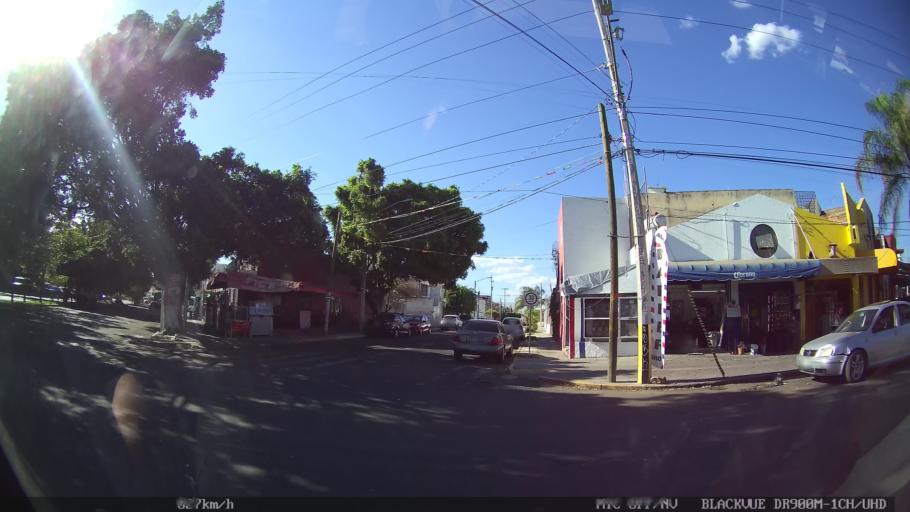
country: MX
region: Jalisco
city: Tlaquepaque
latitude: 20.7122
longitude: -103.3055
